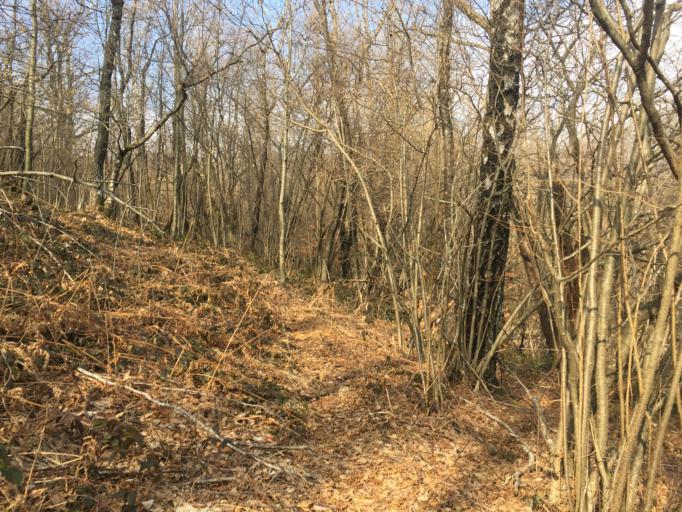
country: IT
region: Friuli Venezia Giulia
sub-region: Provincia di Udine
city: Lusevera
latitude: 46.2576
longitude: 13.2979
